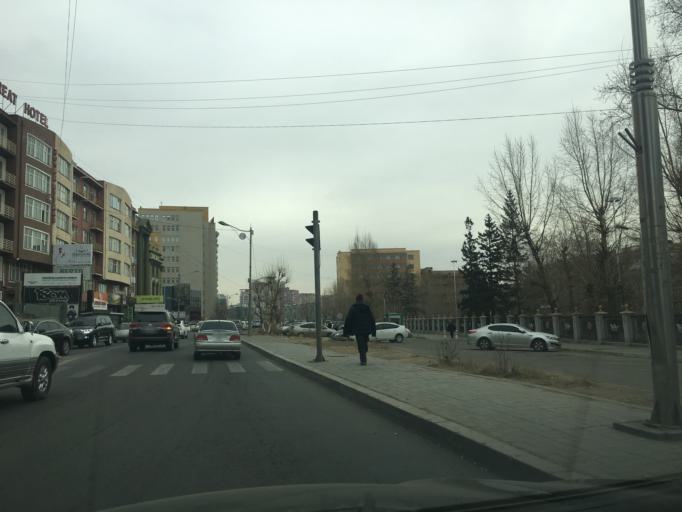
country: MN
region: Ulaanbaatar
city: Ulaanbaatar
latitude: 47.9137
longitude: 106.8913
